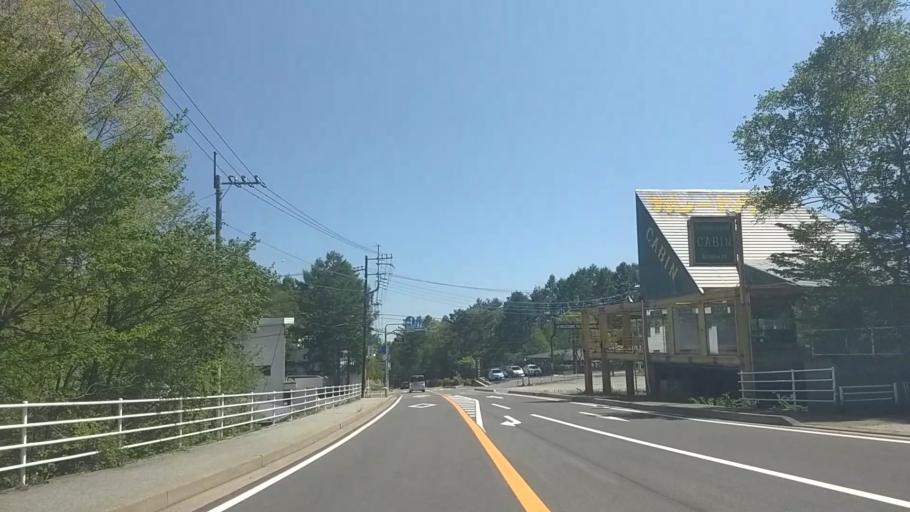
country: JP
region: Yamanashi
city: Nirasaki
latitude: 35.9208
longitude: 138.4404
